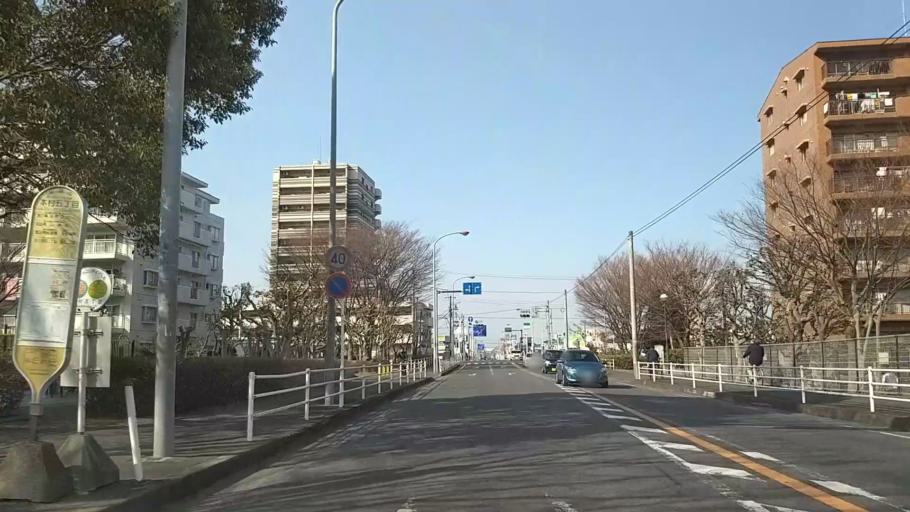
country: JP
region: Kanagawa
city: Chigasaki
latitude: 35.3394
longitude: 139.4133
